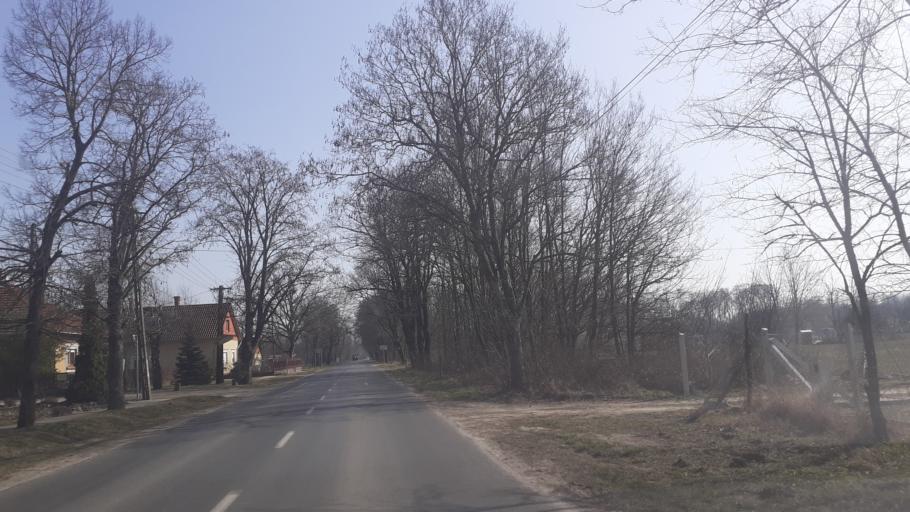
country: HU
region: Bacs-Kiskun
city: Lajosmizse
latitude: 46.9757
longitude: 19.5784
